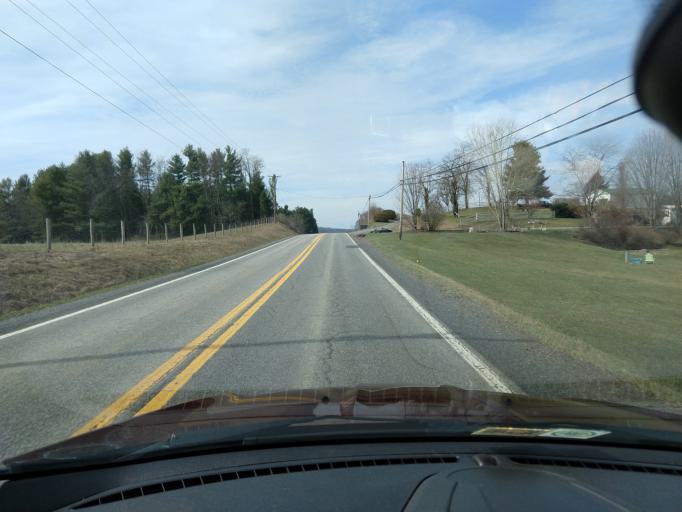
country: US
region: West Virginia
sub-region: Greenbrier County
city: Lewisburg
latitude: 37.9059
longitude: -80.3889
